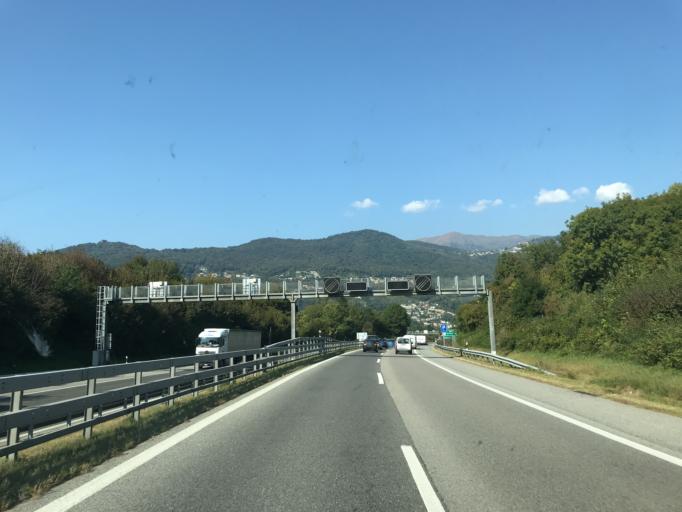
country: CH
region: Ticino
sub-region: Lugano District
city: Montagnola
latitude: 45.9923
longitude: 8.9213
